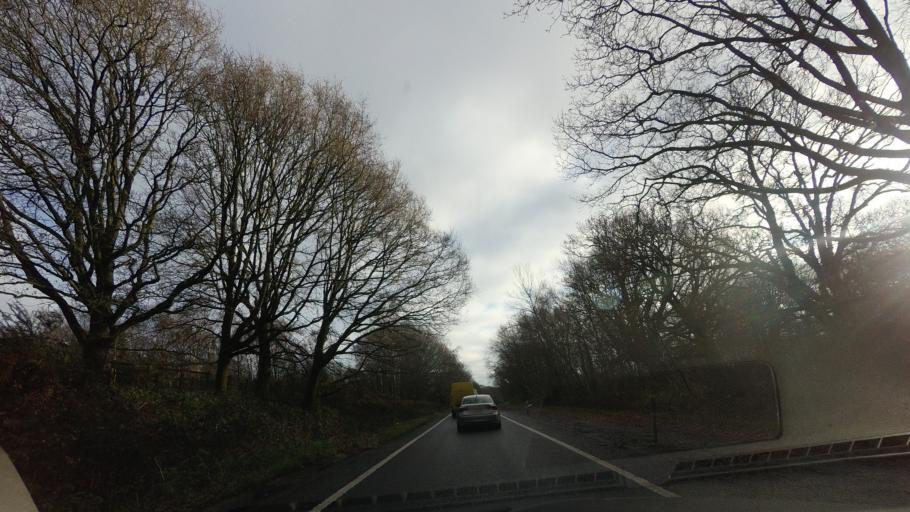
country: GB
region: England
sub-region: Kent
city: Hawkhurst
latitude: 51.0680
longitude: 0.4346
